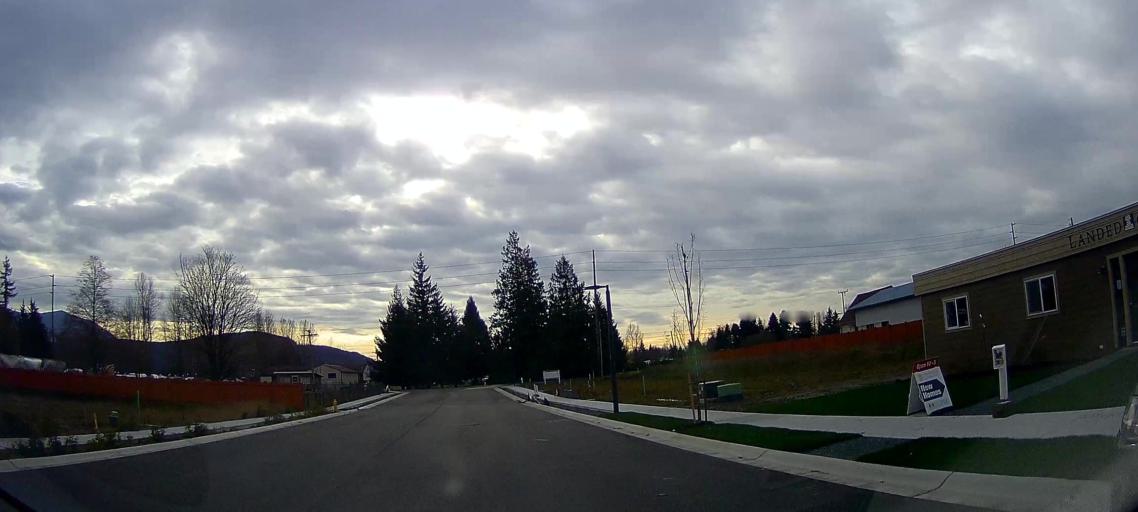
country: US
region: Washington
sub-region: Skagit County
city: Sedro-Woolley
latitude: 48.5156
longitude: -122.2444
